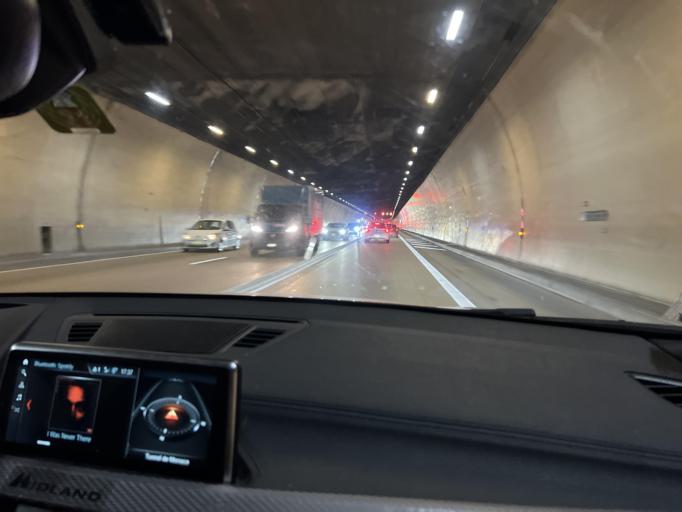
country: FR
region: Provence-Alpes-Cote d'Azur
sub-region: Departement des Alpes-Maritimes
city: La Turbie
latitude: 43.7409
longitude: 7.3845
